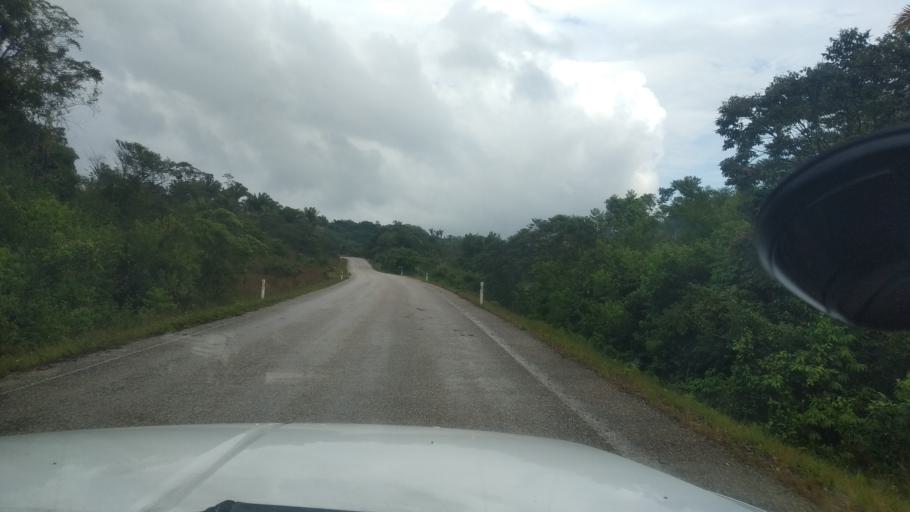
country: GT
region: Peten
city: San Luis
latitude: 16.1893
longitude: -89.1747
